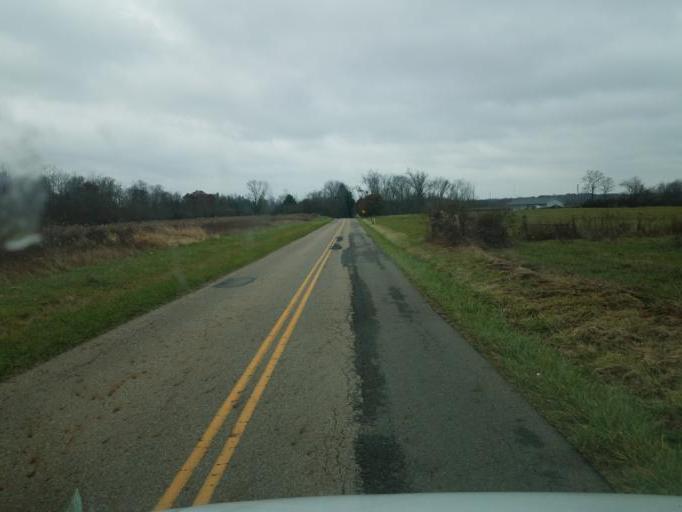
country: US
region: Ohio
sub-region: Knox County
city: Centerburg
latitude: 40.3618
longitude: -82.6230
